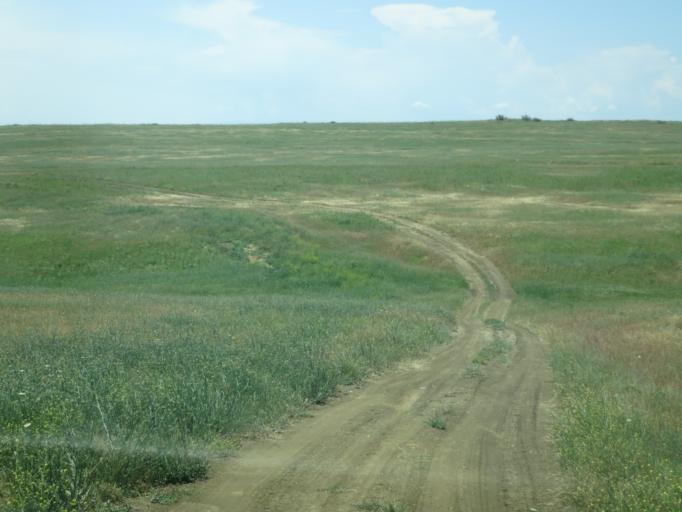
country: AZ
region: Agstafa
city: Saloglu
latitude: 41.4719
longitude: 45.3178
